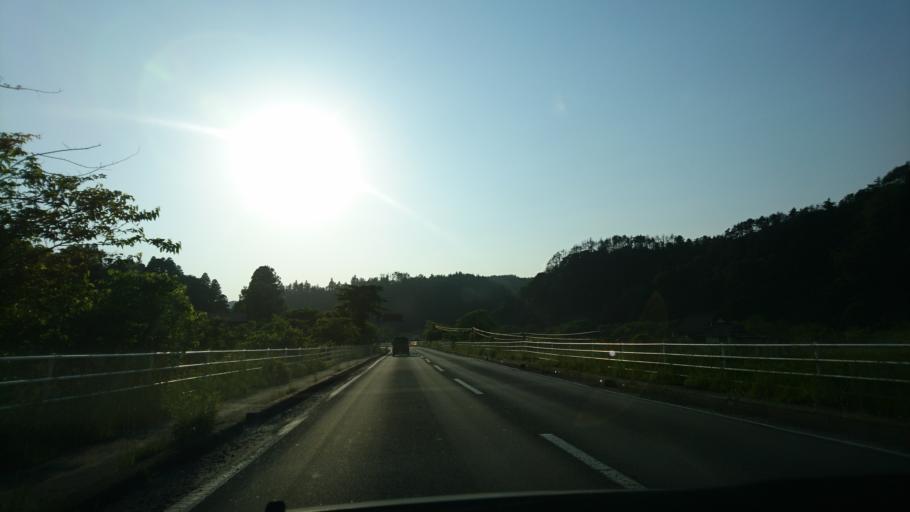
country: JP
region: Iwate
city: Ofunato
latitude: 38.9127
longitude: 141.5385
